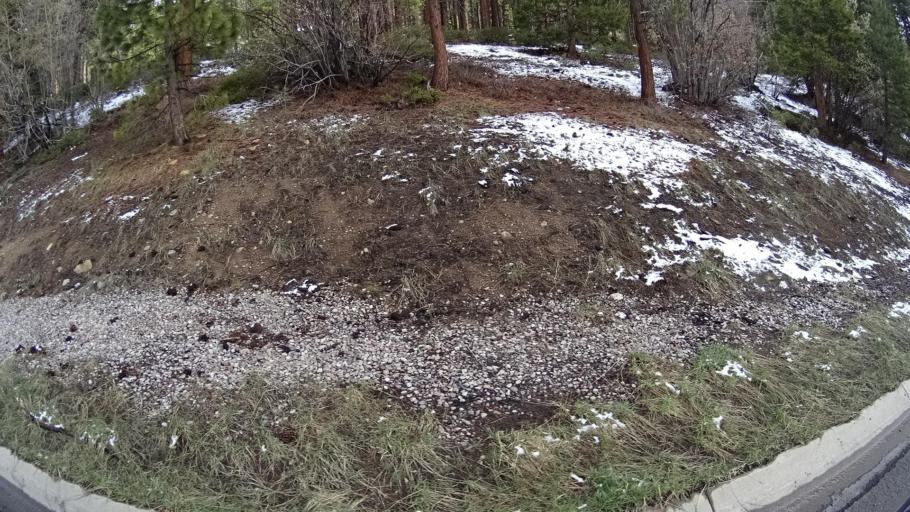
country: US
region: Nevada
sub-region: Washoe County
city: Incline Village
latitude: 39.2648
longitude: -119.9430
